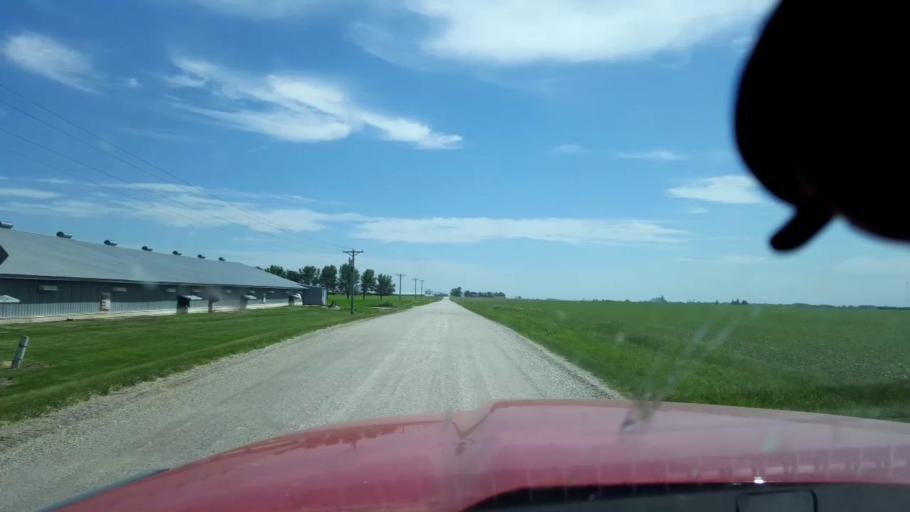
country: US
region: Iowa
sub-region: Hamilton County
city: Jewell
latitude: 42.3521
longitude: -93.5604
